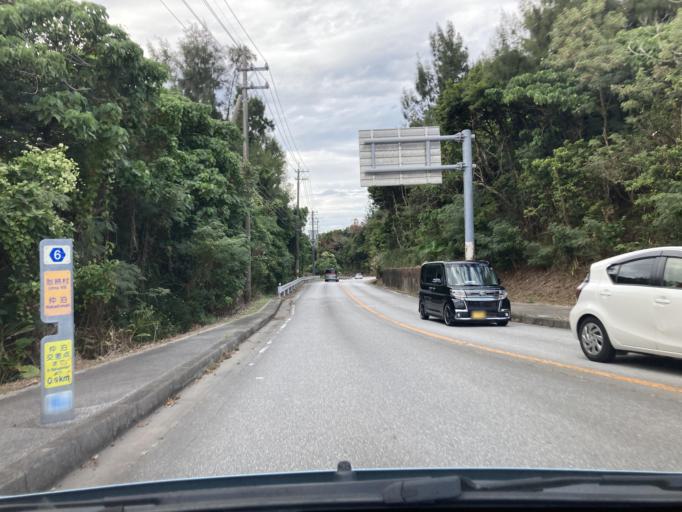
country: JP
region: Okinawa
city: Ishikawa
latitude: 26.4345
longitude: 127.8074
